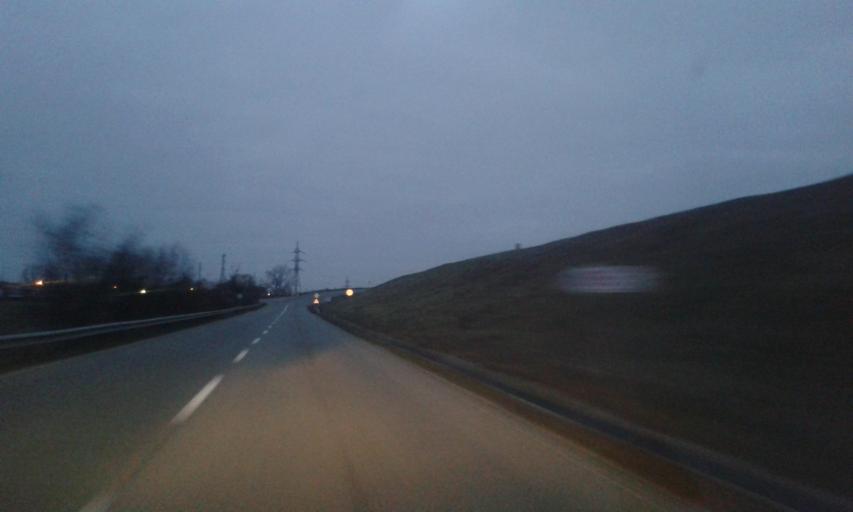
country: RO
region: Gorj
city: Targu Jiu
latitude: 45.0602
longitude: 23.2733
